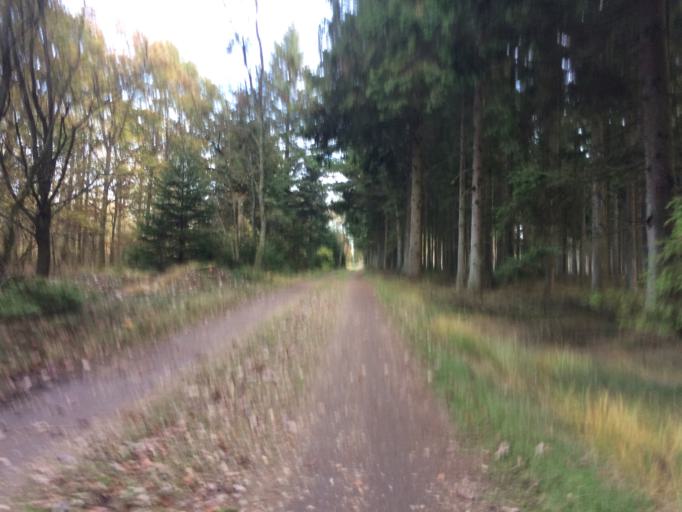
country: DK
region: Central Jutland
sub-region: Holstebro Kommune
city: Ulfborg
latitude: 56.2132
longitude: 8.4564
